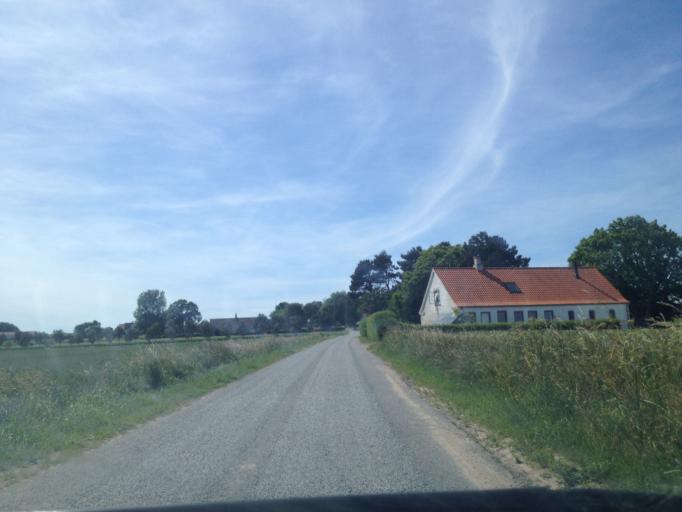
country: DK
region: Central Jutland
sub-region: Samso Kommune
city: Tranebjerg
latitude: 55.9511
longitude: 10.5535
